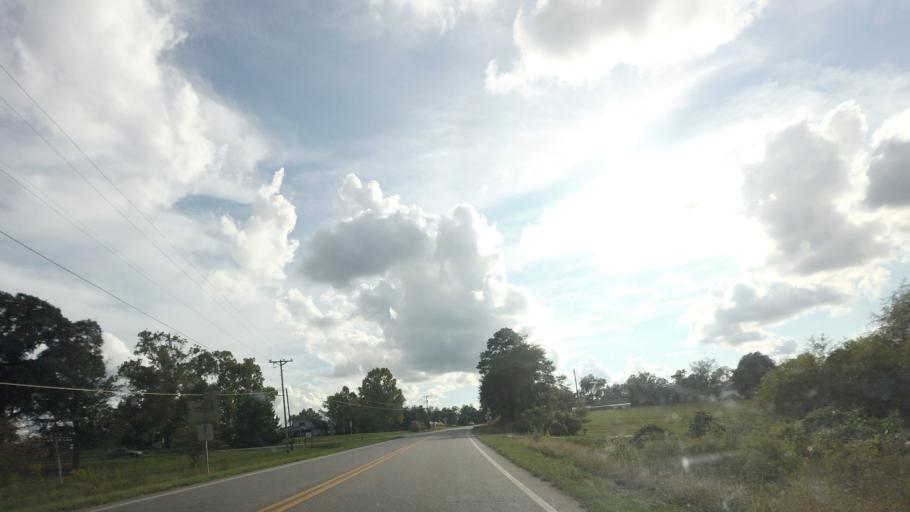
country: US
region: Georgia
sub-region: Pulaski County
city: Hawkinsville
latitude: 32.2938
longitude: -83.4340
